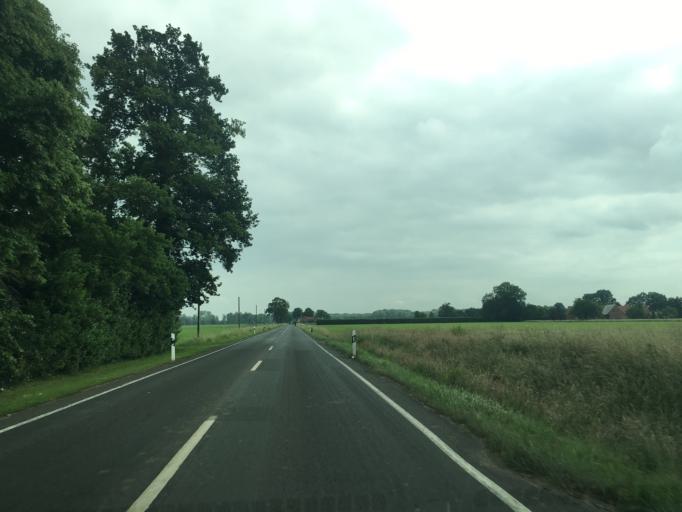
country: DE
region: North Rhine-Westphalia
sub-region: Regierungsbezirk Munster
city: Steinfurt
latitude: 52.1099
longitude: 7.3387
